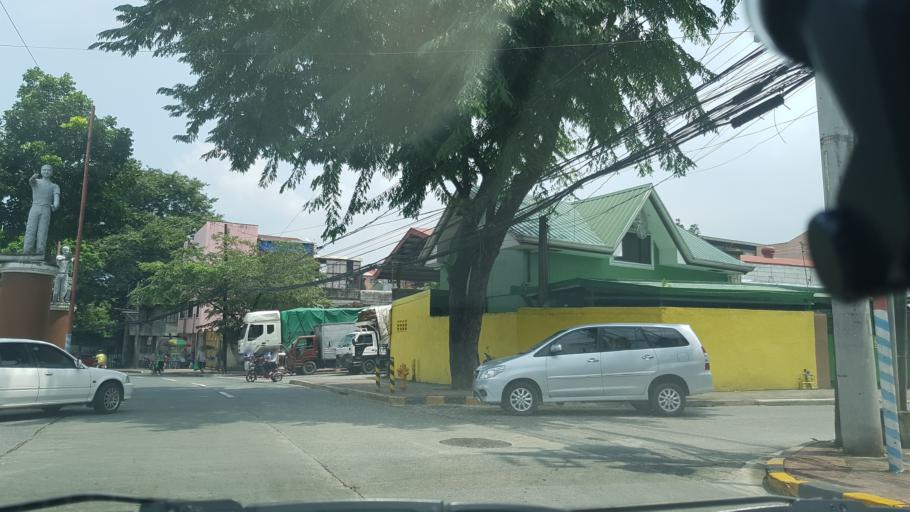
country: PH
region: Calabarzon
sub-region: Province of Rizal
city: Antipolo
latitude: 14.6480
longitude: 121.1161
